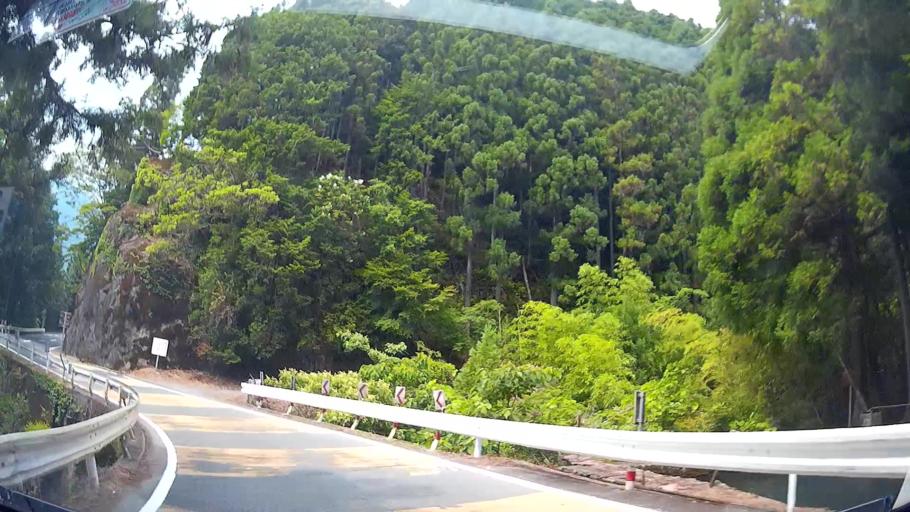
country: JP
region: Shizuoka
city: Mori
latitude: 35.0879
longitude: 137.8348
